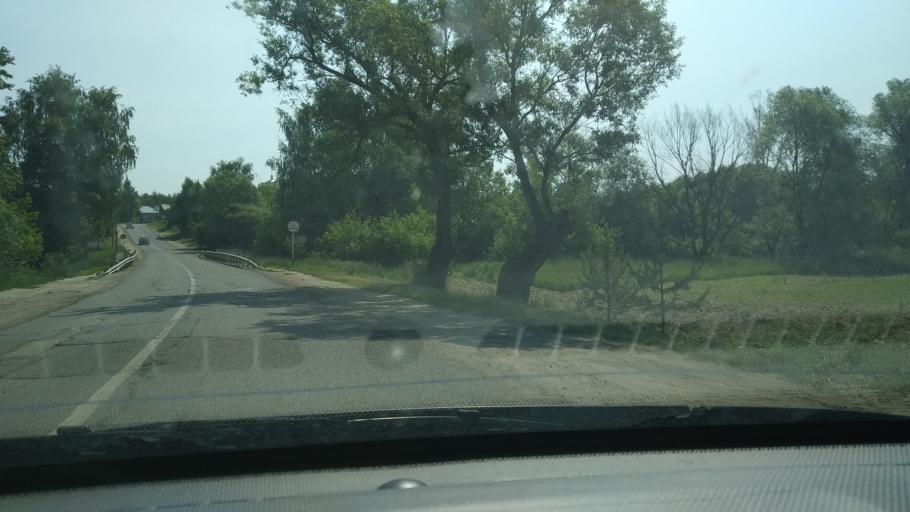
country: RU
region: Tatarstan
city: Osinovo
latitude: 55.9819
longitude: 48.7986
